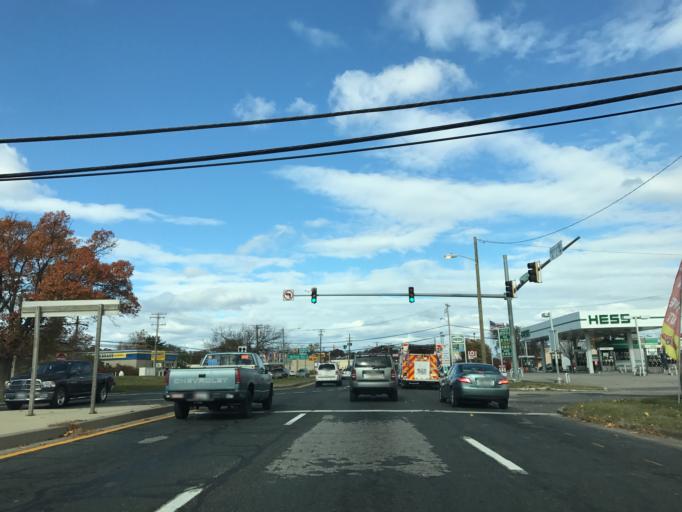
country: US
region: Maryland
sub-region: Anne Arundel County
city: Ferndale
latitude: 39.1877
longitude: -76.6131
